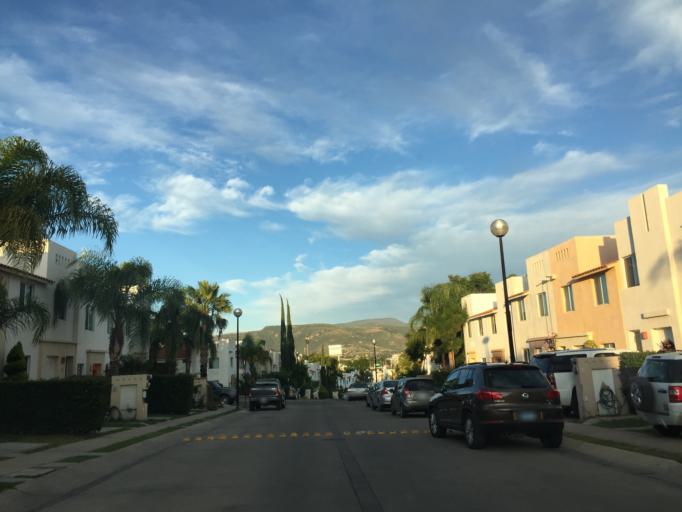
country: MX
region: Guanajuato
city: Leon
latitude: 21.1716
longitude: -101.6746
